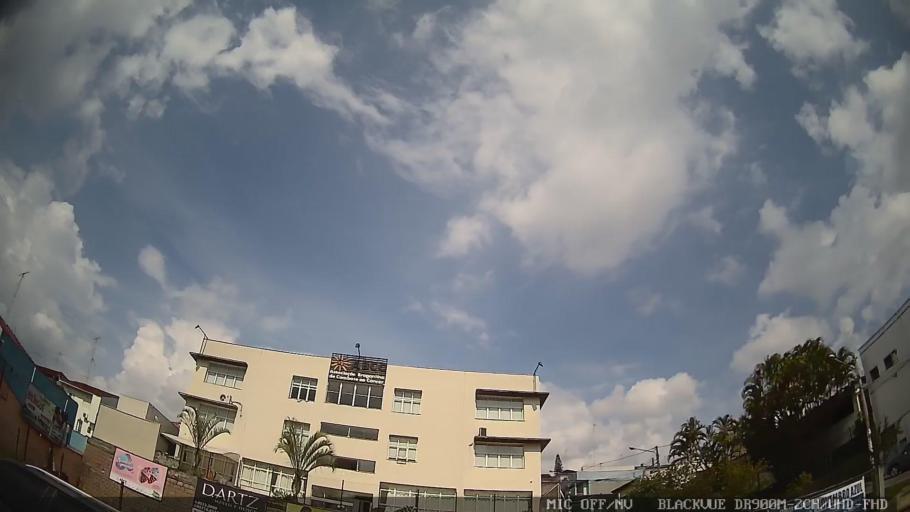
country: BR
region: Sao Paulo
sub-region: Braganca Paulista
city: Braganca Paulista
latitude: -22.9530
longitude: -46.5449
